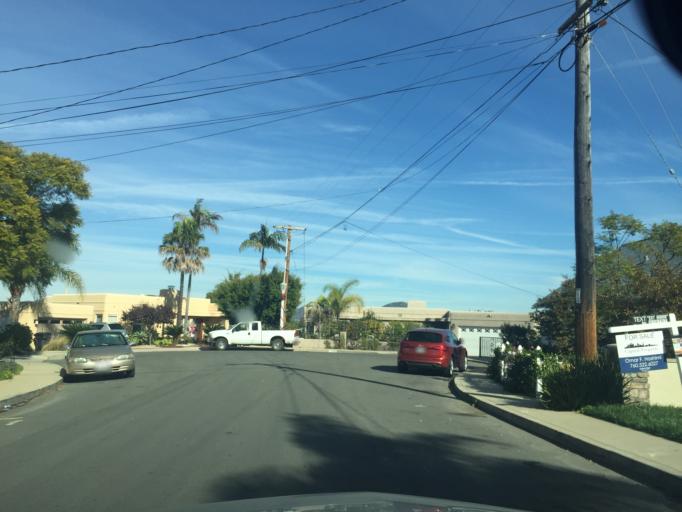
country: US
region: California
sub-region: San Diego County
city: Lemon Grove
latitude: 32.7729
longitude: -117.1002
